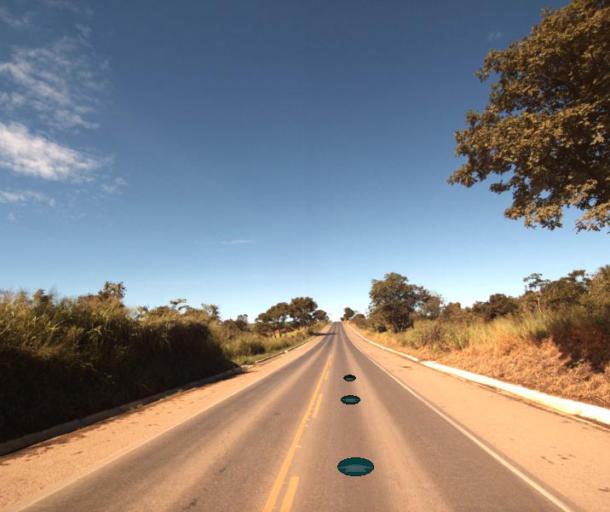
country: BR
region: Goias
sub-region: Itapaci
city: Itapaci
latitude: -14.8739
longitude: -49.3330
